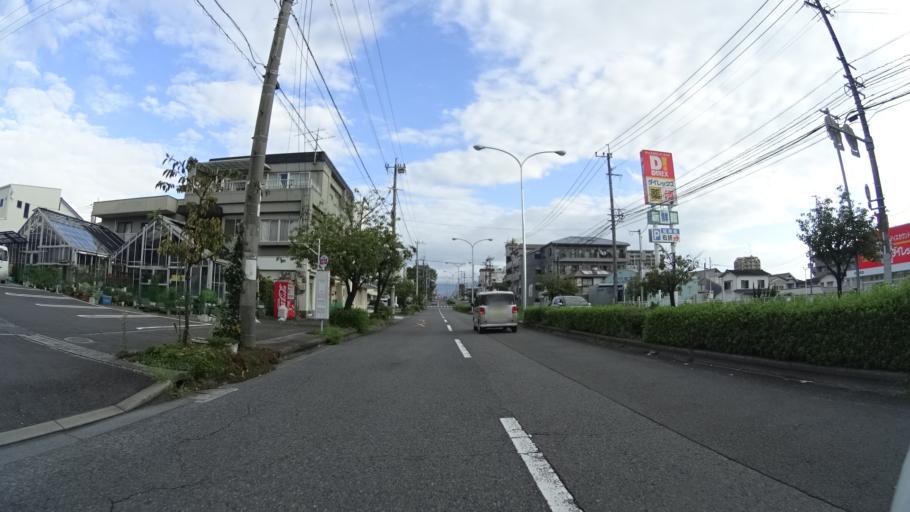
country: JP
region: Oita
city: Beppu
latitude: 33.2859
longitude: 131.4965
